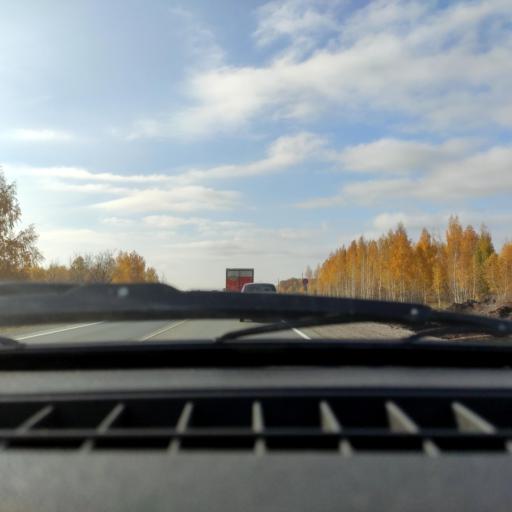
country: RU
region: Bashkortostan
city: Kabakovo
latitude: 54.7203
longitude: 56.2380
